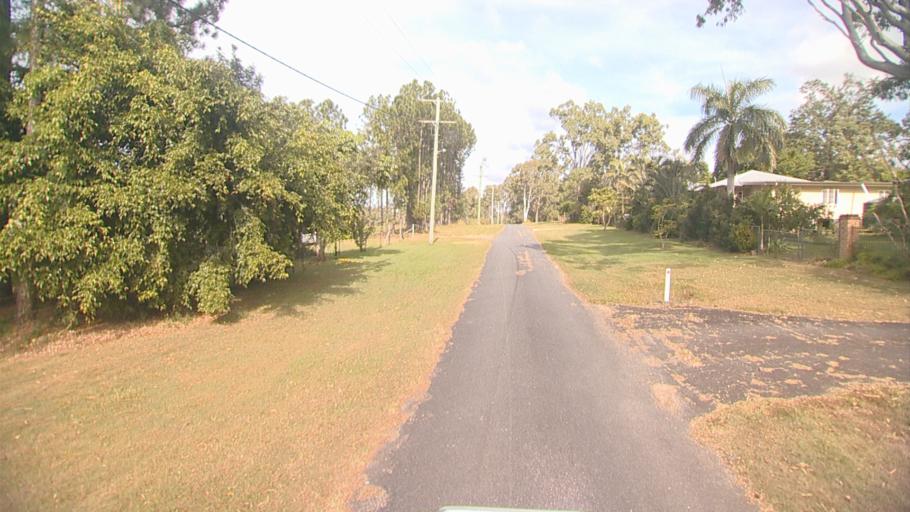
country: AU
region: Queensland
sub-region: Logan
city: Waterford West
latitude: -27.6930
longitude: 153.1620
